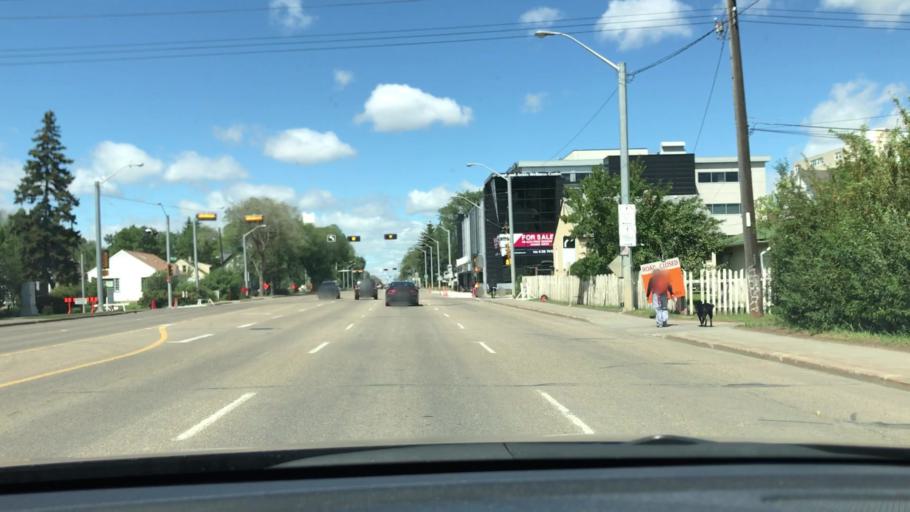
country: CA
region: Alberta
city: Edmonton
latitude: 53.5116
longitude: -113.5118
